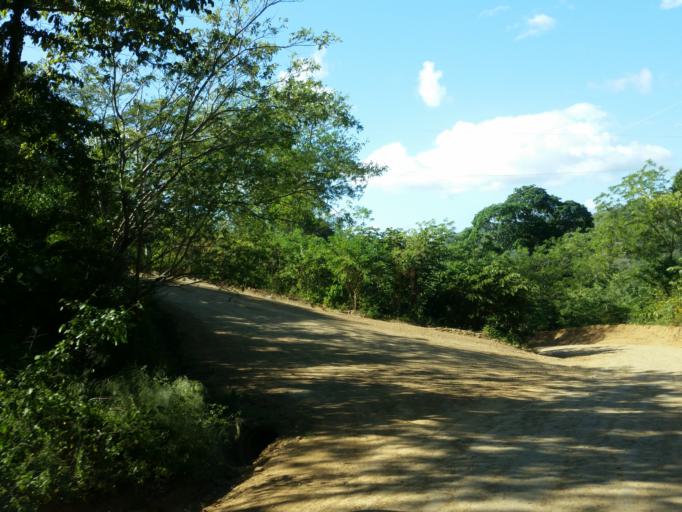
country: NI
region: Rivas
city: San Juan del Sur
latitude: 11.1846
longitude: -85.7998
